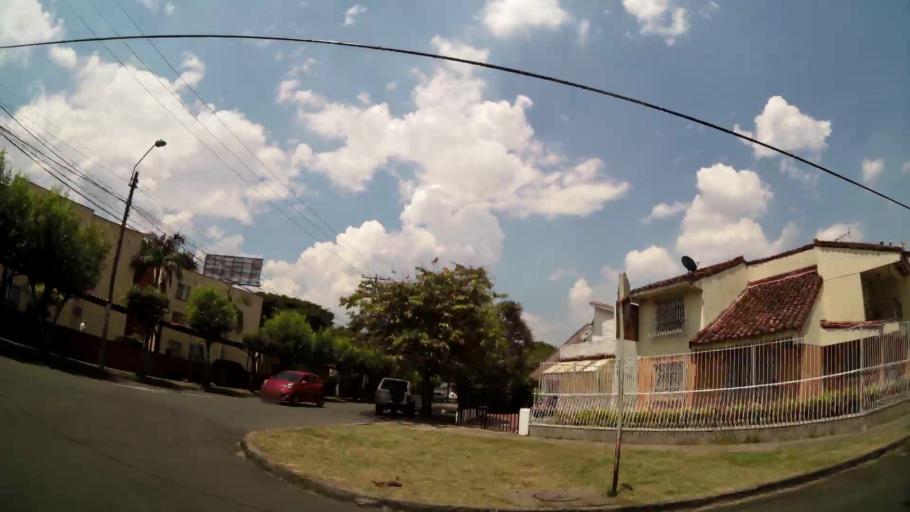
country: CO
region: Valle del Cauca
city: Cali
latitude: 3.4163
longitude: -76.5436
